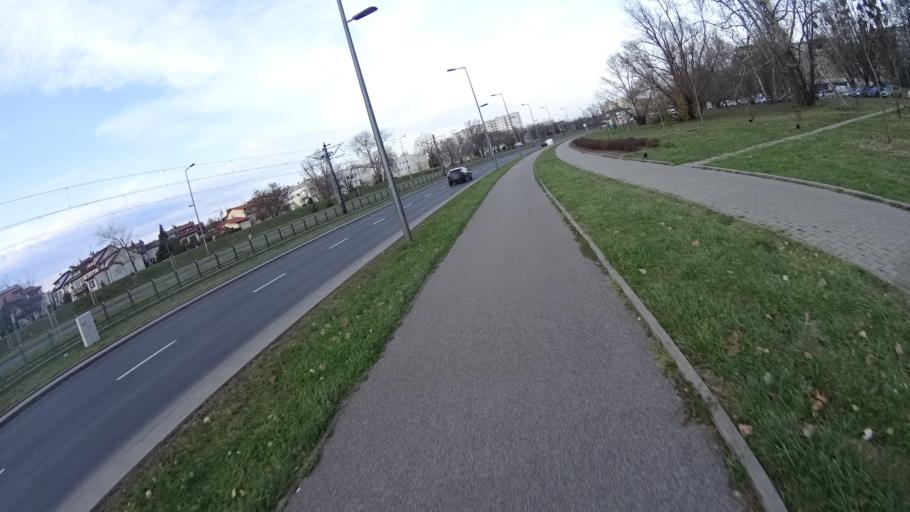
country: PL
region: Masovian Voivodeship
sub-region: Warszawa
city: Bemowo
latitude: 52.2486
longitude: 20.9112
